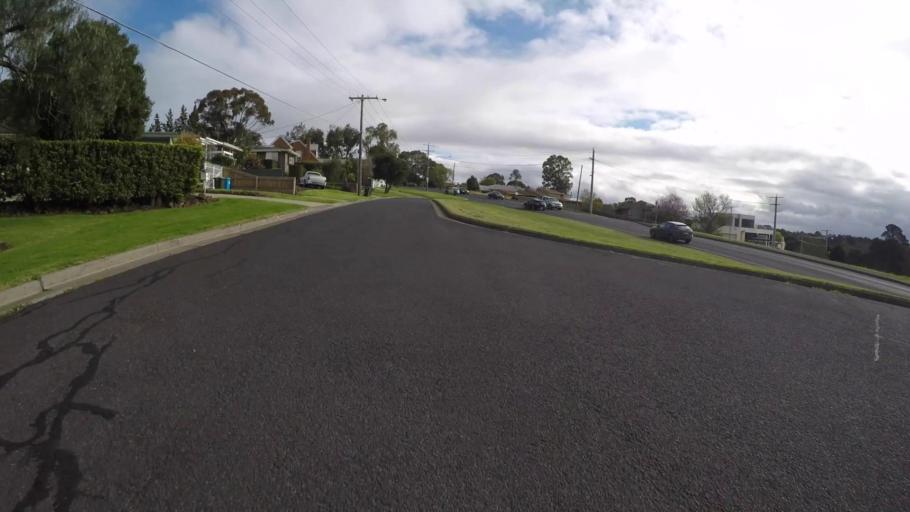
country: AU
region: Victoria
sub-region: Greater Geelong
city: Wandana Heights
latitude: -38.1495
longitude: 144.3156
